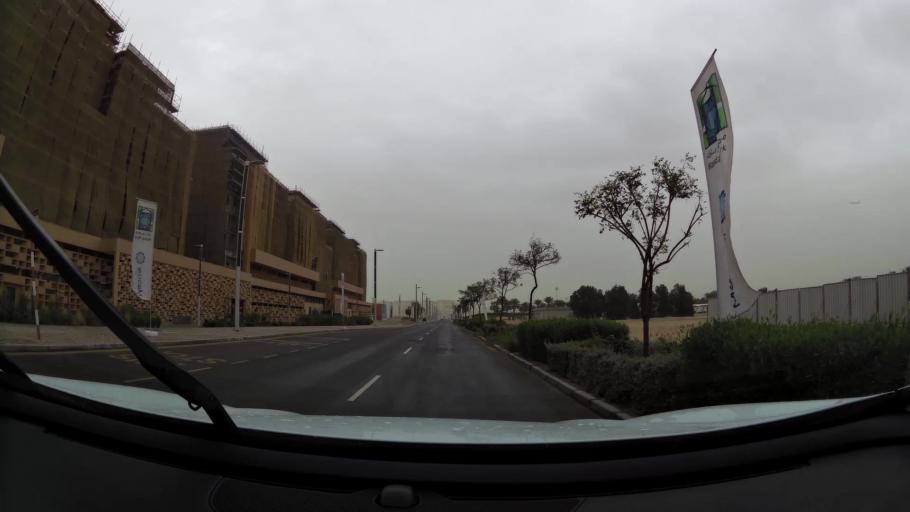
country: AE
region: Abu Dhabi
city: Abu Dhabi
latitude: 24.4356
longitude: 54.6213
